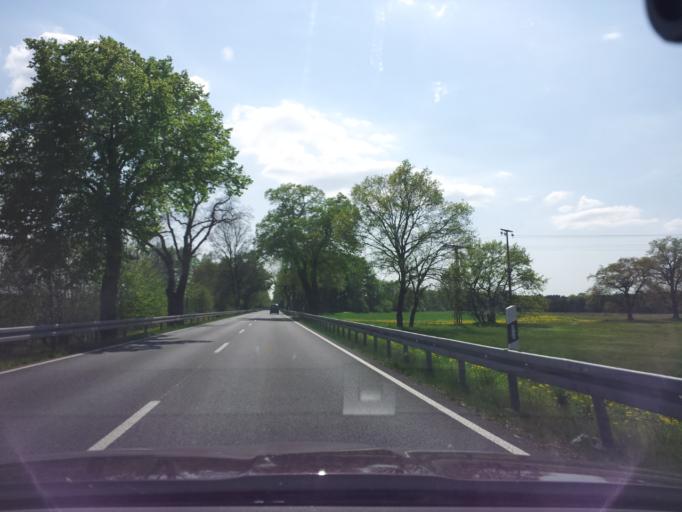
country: DE
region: Brandenburg
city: Treuenbrietzen
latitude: 52.1281
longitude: 12.9032
